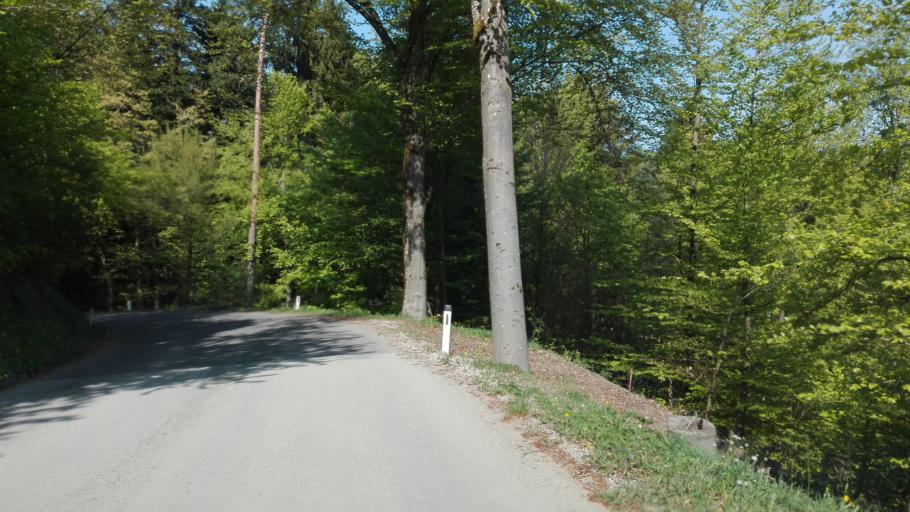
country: AT
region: Upper Austria
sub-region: Politischer Bezirk Rohrbach
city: Atzesberg
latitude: 48.4262
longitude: 13.9201
